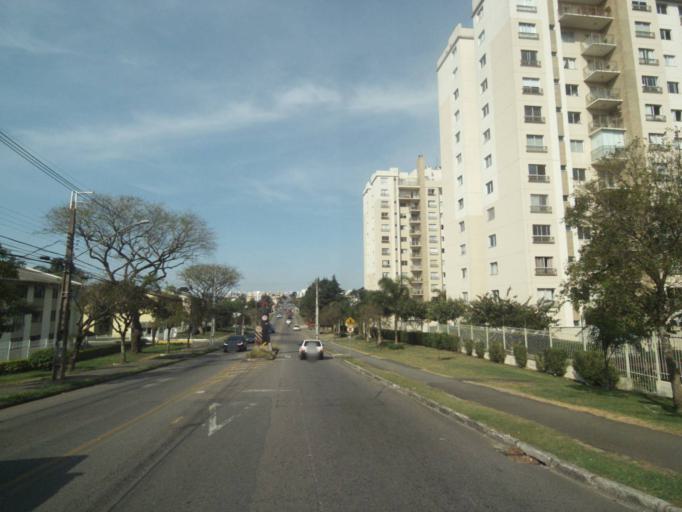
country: BR
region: Parana
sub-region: Curitiba
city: Curitiba
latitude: -25.4602
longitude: -49.3209
